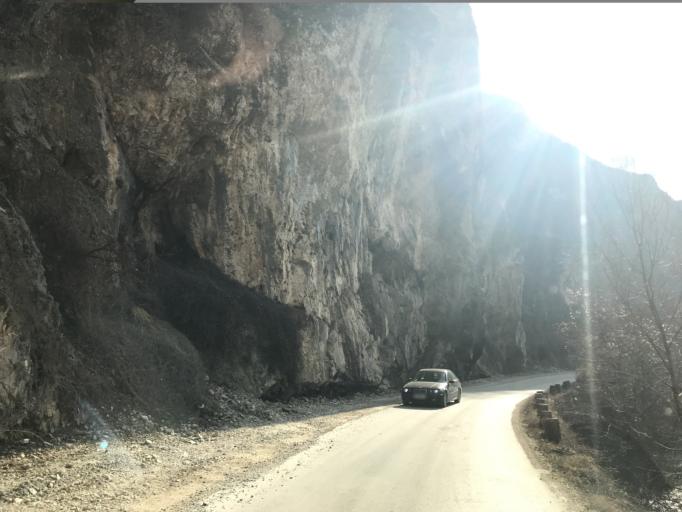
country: XK
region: Prizren
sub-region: Prizren
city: Prizren
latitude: 42.2089
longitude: 20.7512
